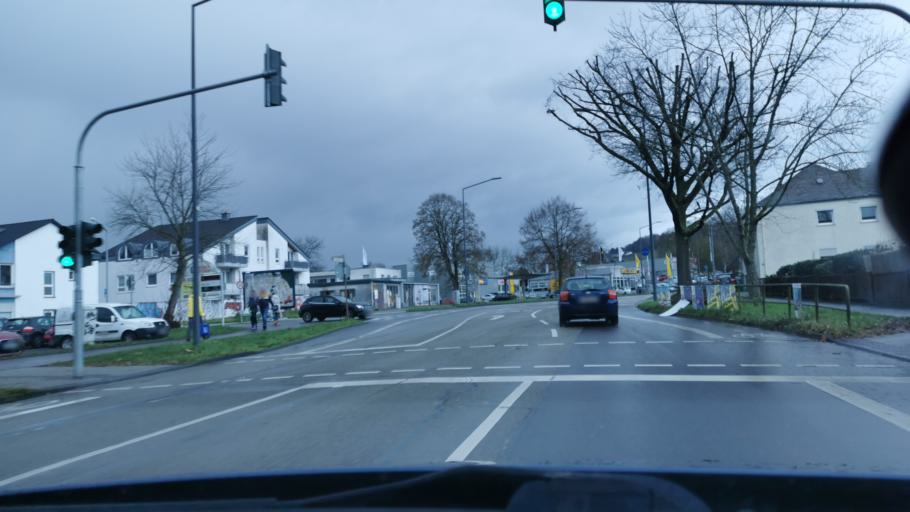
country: DE
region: Rheinland-Pfalz
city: Trier
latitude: 49.7408
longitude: 6.6430
